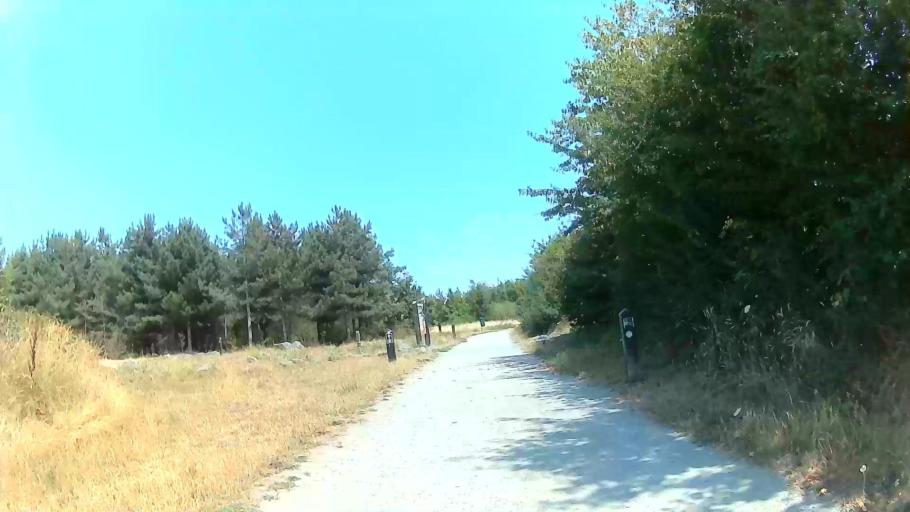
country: GB
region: England
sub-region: Greater London
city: Elm Park
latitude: 51.5302
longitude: 0.1975
